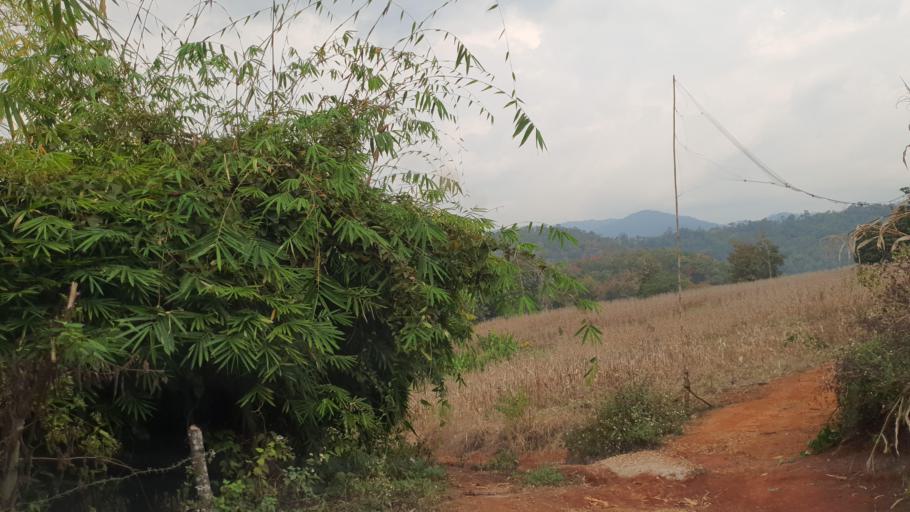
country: TH
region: Chiang Mai
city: Mae Wang
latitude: 18.6568
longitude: 98.6507
